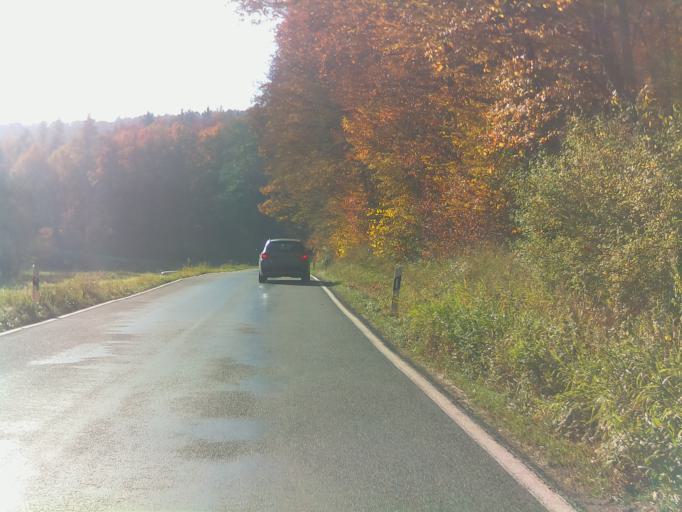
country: DE
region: Bavaria
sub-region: Regierungsbezirk Unterfranken
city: Michelau
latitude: 49.8585
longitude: 10.4967
